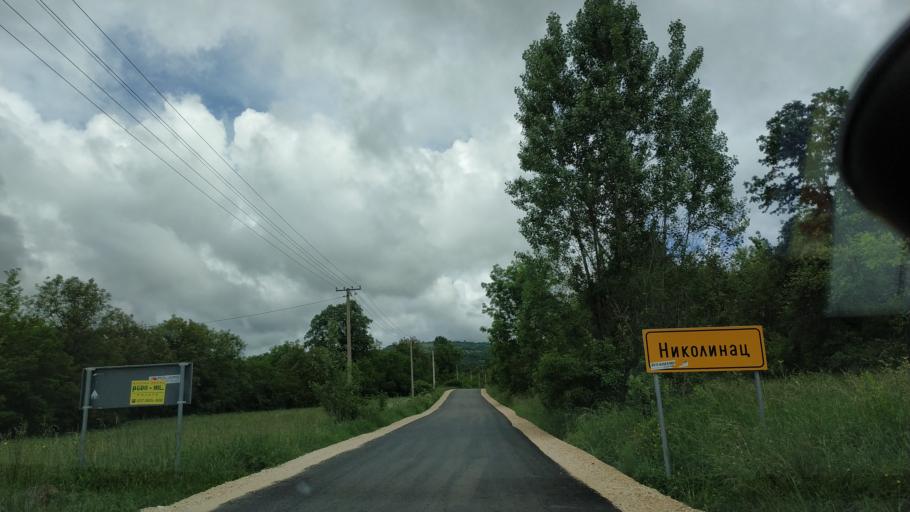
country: RS
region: Central Serbia
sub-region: Zajecarski Okrug
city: Soko Banja
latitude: 43.6675
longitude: 21.9114
